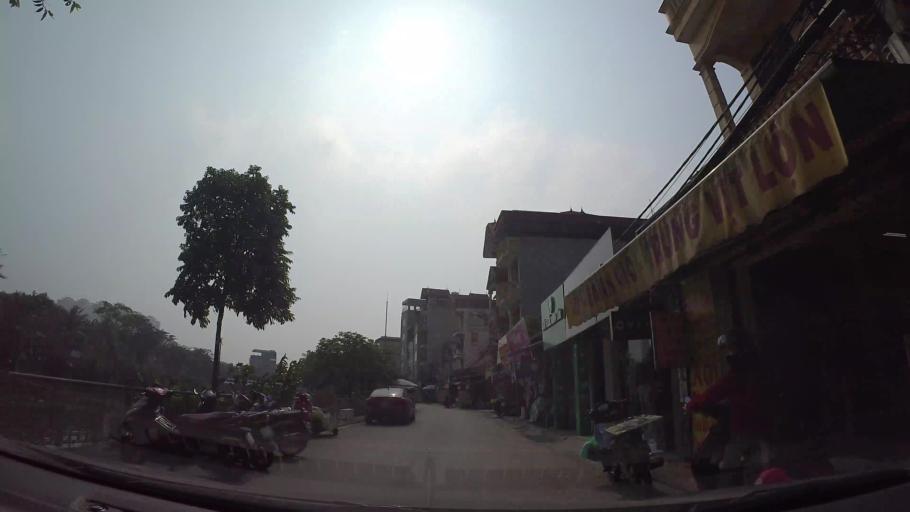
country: VN
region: Ha Noi
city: Van Dien
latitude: 20.9713
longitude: 105.8348
